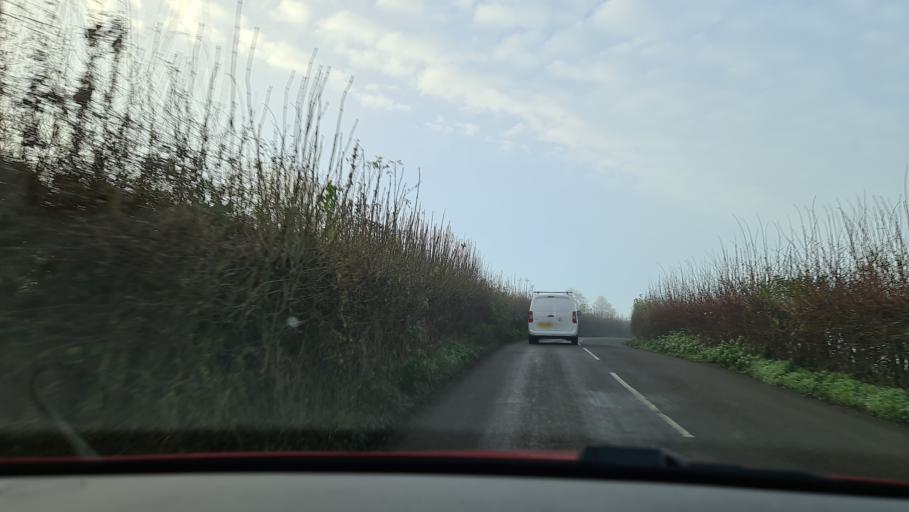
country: GB
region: England
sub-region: Buckinghamshire
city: Waddesdon
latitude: 51.8312
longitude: -0.9579
